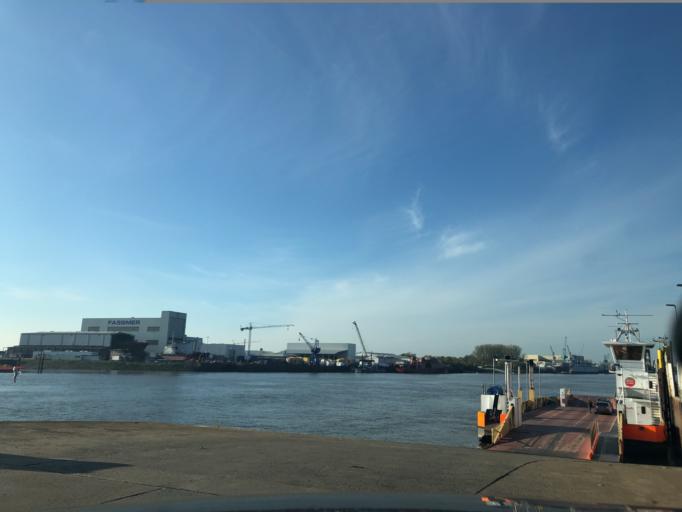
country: DE
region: Lower Saxony
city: Lemwerder
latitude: 53.1819
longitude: 8.5616
